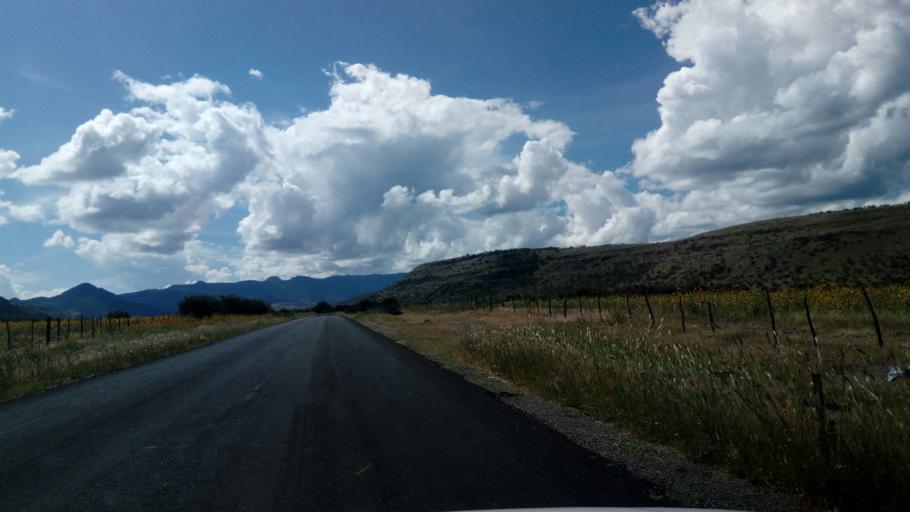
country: MX
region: Durango
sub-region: Durango
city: Jose Refugio Salcido
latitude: 23.8257
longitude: -104.4820
